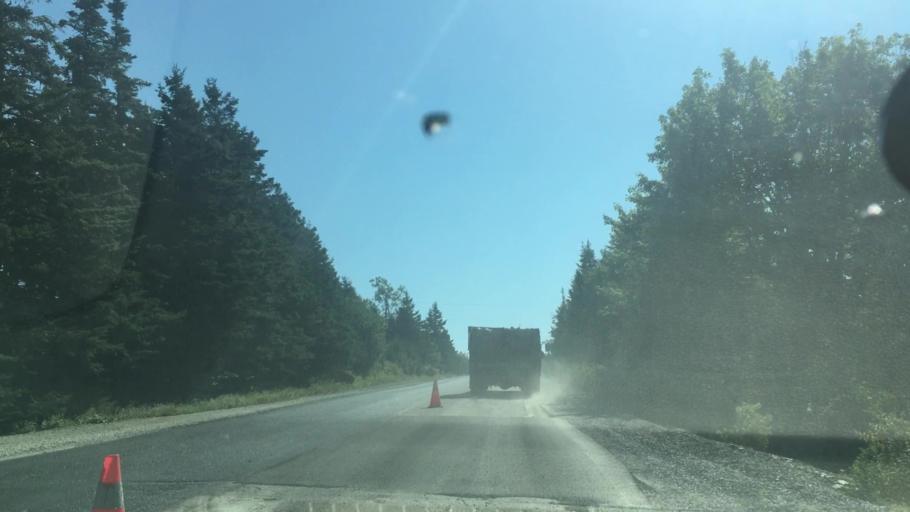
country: CA
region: Nova Scotia
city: New Glasgow
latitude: 44.9064
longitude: -62.4909
